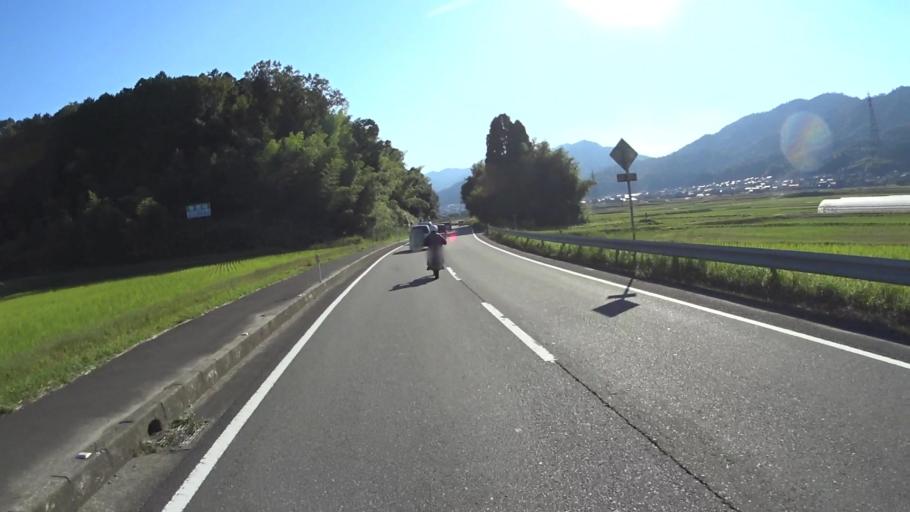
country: JP
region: Kyoto
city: Miyazu
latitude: 35.4948
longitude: 135.1009
